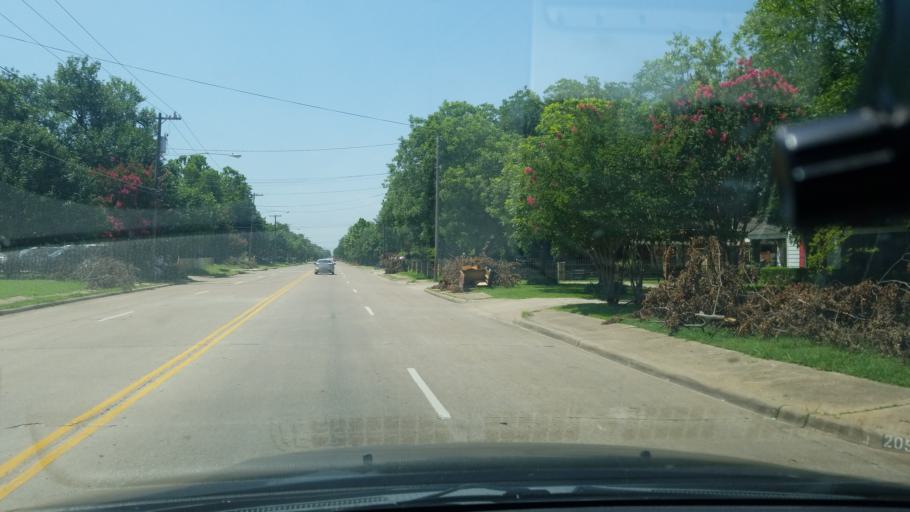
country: US
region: Texas
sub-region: Dallas County
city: Balch Springs
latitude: 32.7483
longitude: -96.6786
